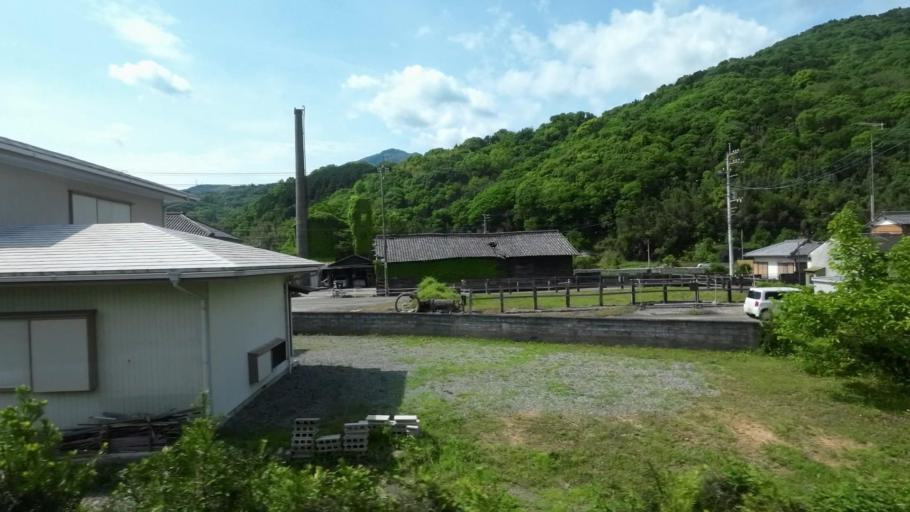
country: JP
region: Tokushima
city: Wakimachi
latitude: 34.0618
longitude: 134.2007
